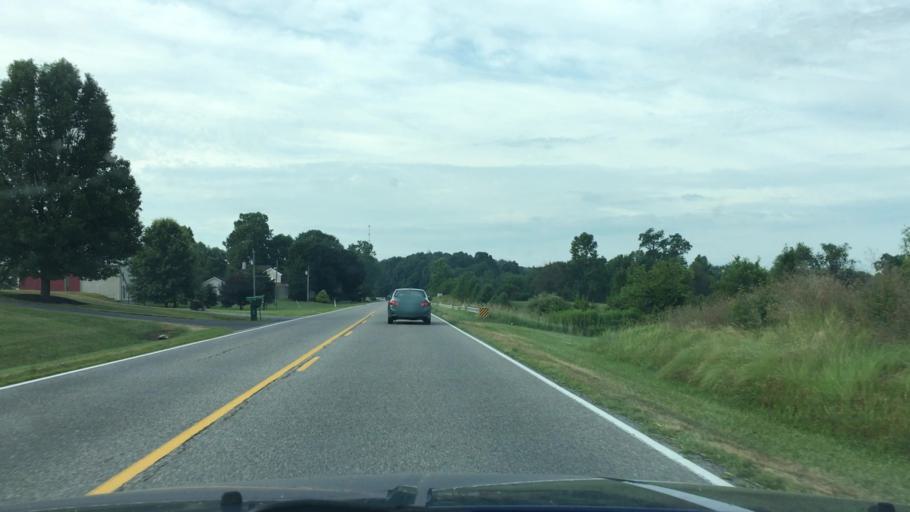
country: US
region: Virginia
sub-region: Augusta County
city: Dooms
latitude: 38.1301
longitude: -78.9143
